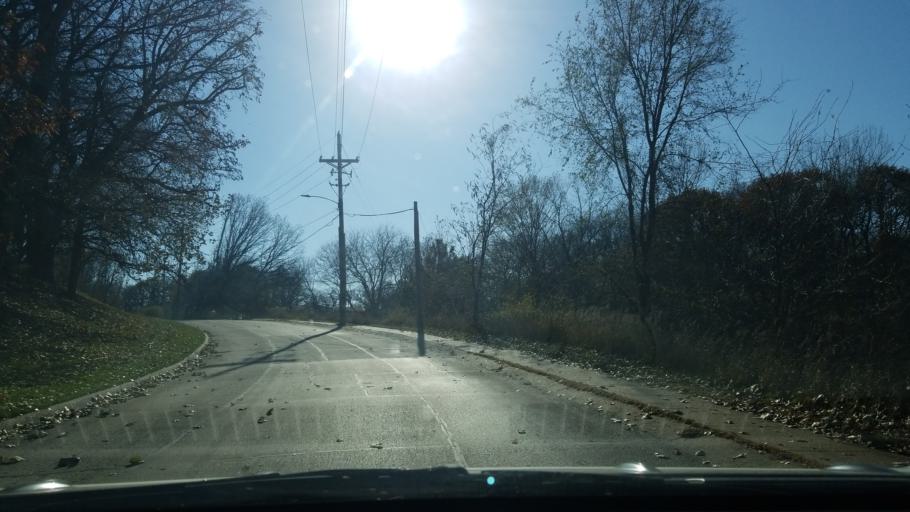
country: US
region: Nebraska
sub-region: Sarpy County
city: Bellevue
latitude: 41.1618
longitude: -95.9020
